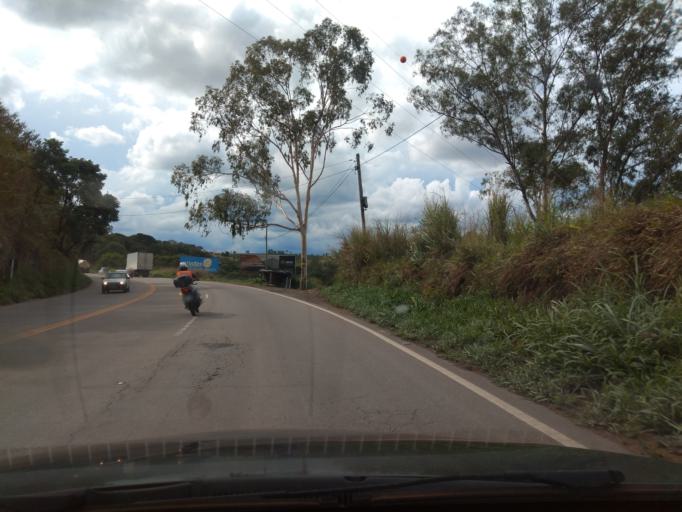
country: BR
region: Minas Gerais
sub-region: Varginha
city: Varginha
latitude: -21.6046
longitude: -45.4318
